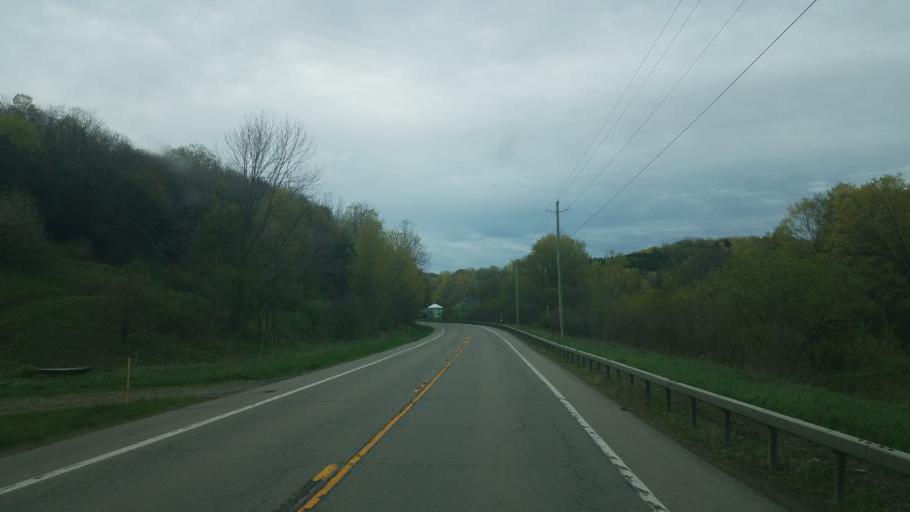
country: US
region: New York
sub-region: Steuben County
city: Canisteo
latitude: 42.1760
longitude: -77.5322
